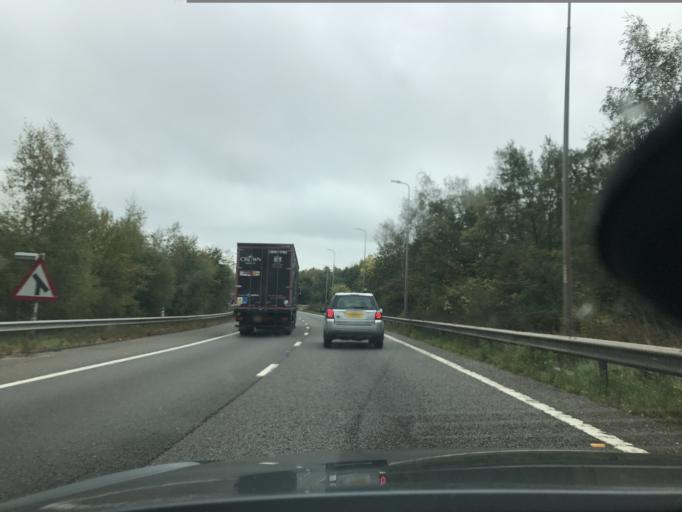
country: GB
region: England
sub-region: Solihull
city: Cheswick Green
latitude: 52.3486
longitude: -1.8069
